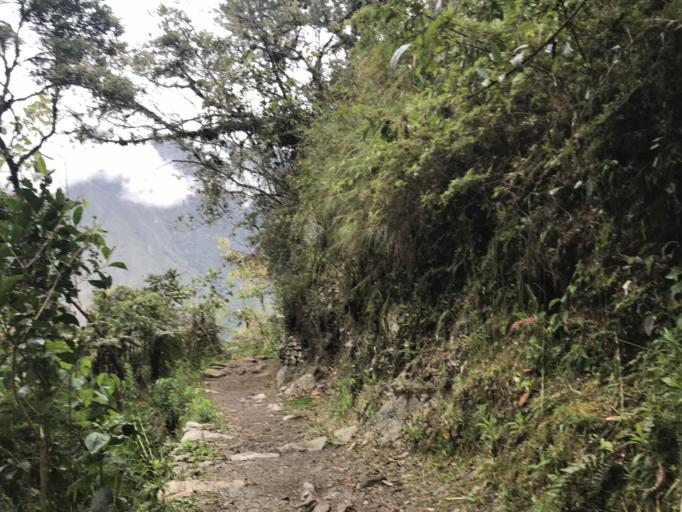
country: PE
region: Cusco
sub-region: Provincia de La Convencion
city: Santa Teresa
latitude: -13.1728
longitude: -72.5335
